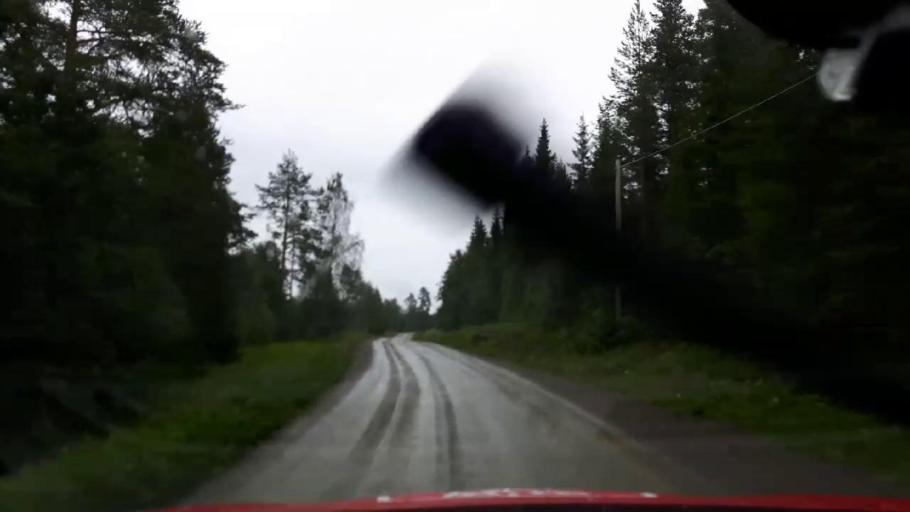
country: SE
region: Jaemtland
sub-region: OEstersunds Kommun
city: Brunflo
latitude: 62.8830
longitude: 14.8759
